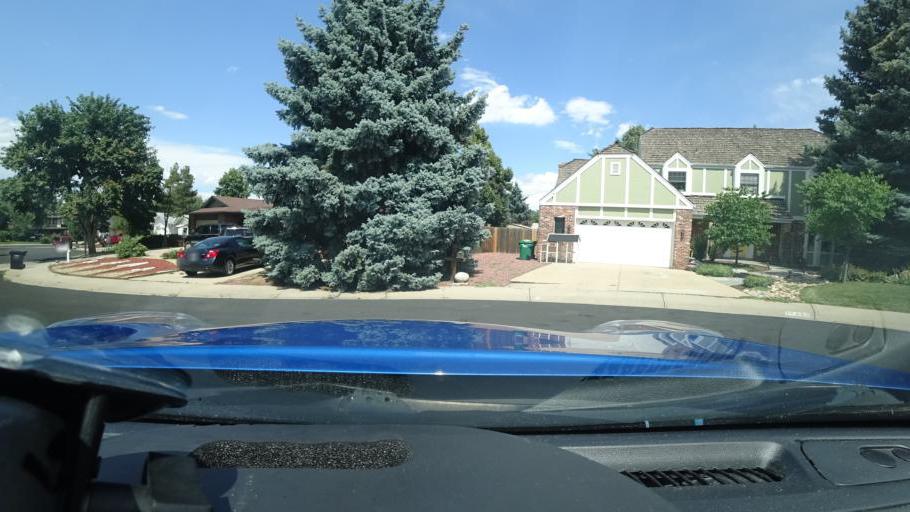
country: US
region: Colorado
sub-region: Adams County
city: Aurora
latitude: 39.7118
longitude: -104.8397
